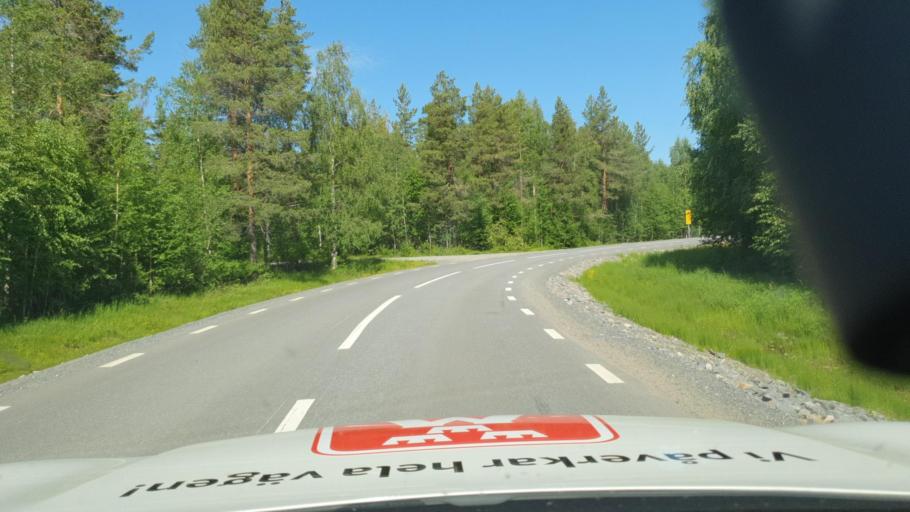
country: SE
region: Vaesterbotten
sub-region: Skelleftea Kommun
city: Langsele
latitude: 64.7745
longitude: 20.3376
